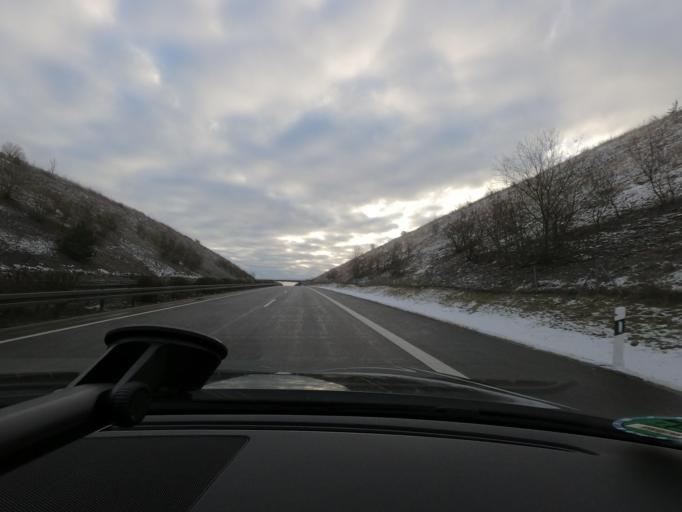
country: DE
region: Thuringia
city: Veilsdorf
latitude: 50.4674
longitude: 10.8343
